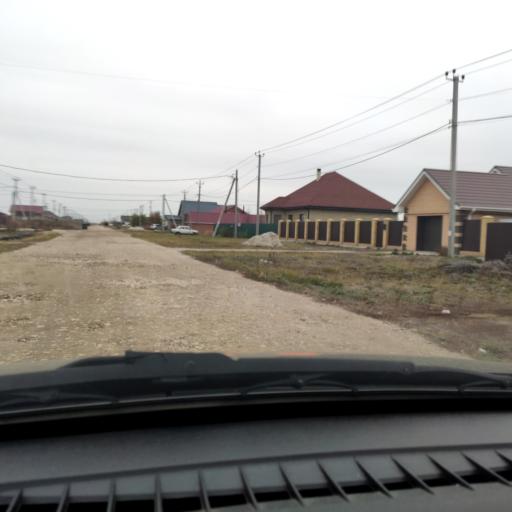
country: RU
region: Samara
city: Podstepki
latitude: 53.5258
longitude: 49.1543
